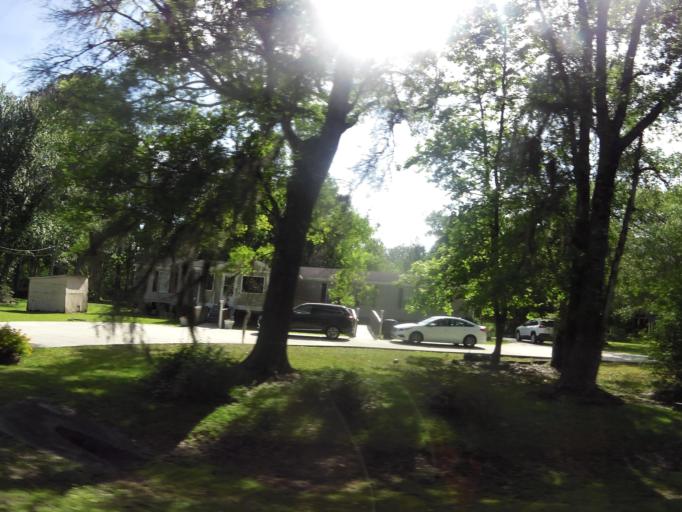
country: US
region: Florida
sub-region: Nassau County
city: Callahan
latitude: 30.5739
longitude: -81.8451
